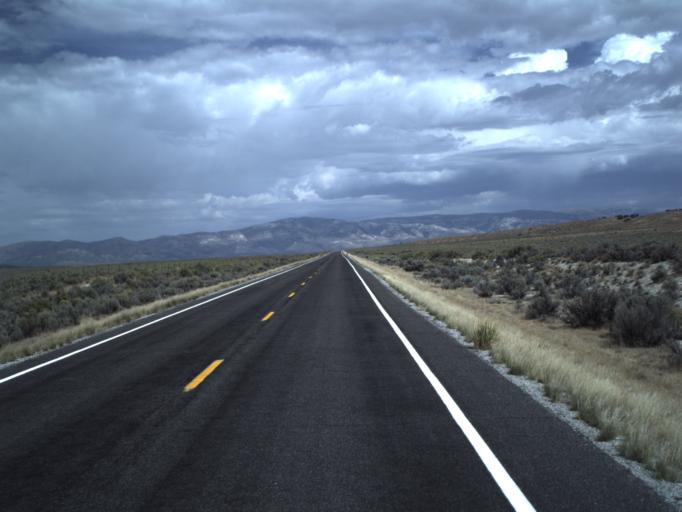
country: US
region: Idaho
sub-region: Cassia County
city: Burley
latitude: 41.6706
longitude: -113.5443
